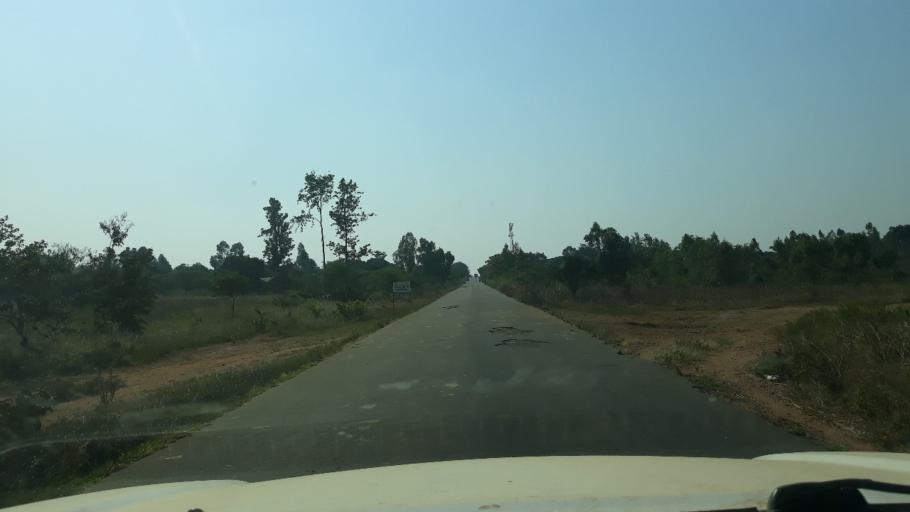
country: BI
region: Cibitoke
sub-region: Commune of Buganda
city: Buganda
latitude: -3.0000
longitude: 29.0974
